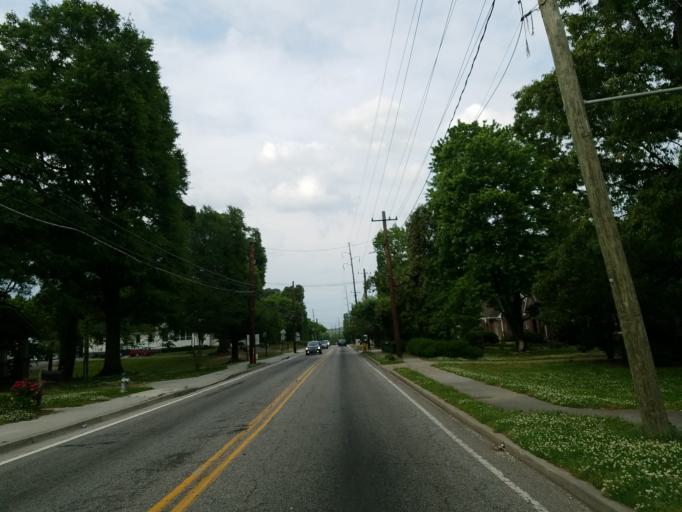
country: US
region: Georgia
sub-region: Cobb County
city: Vinings
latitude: 33.8154
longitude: -84.4666
